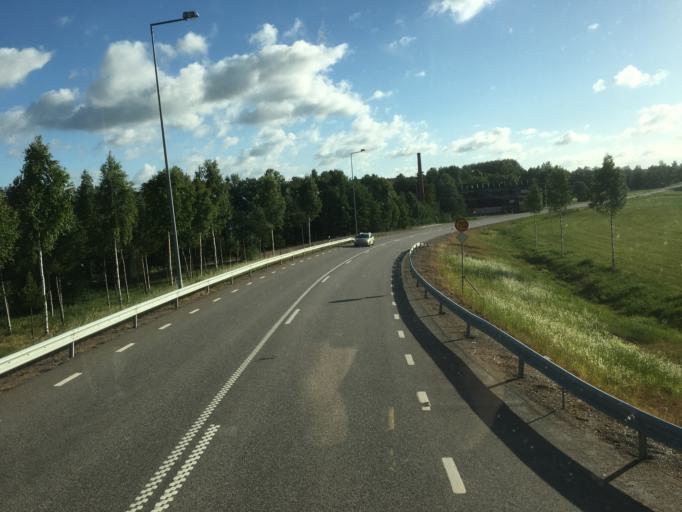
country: SE
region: Gaevleborg
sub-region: Sandvikens Kommun
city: Jarbo
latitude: 60.5683
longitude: 16.4908
